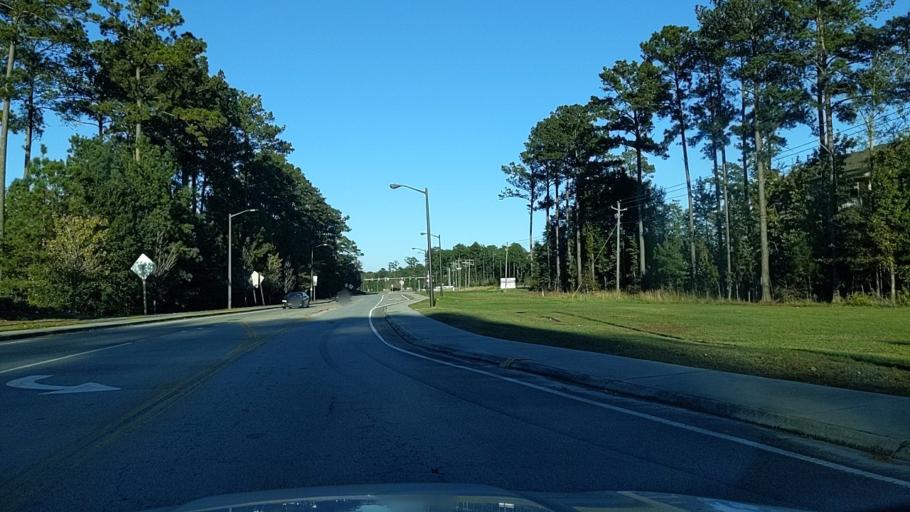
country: US
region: Georgia
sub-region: Chatham County
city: Pooler
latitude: 32.1757
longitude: -81.2315
